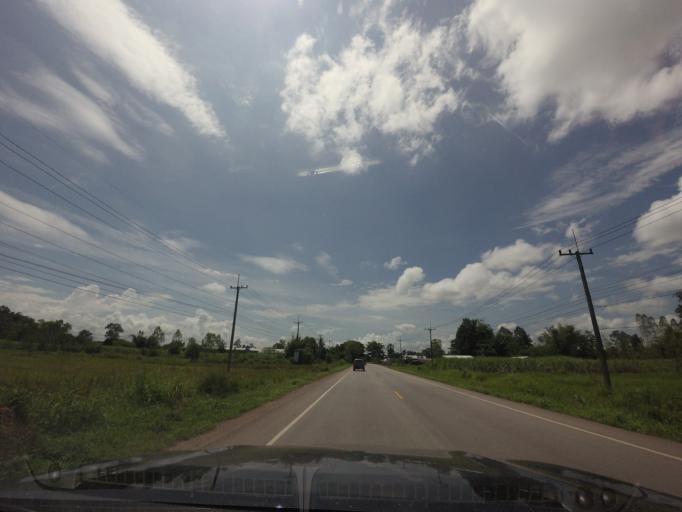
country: TH
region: Changwat Udon Thani
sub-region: Amphoe Ban Phue
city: Ban Phue
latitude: 17.7360
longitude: 102.3969
